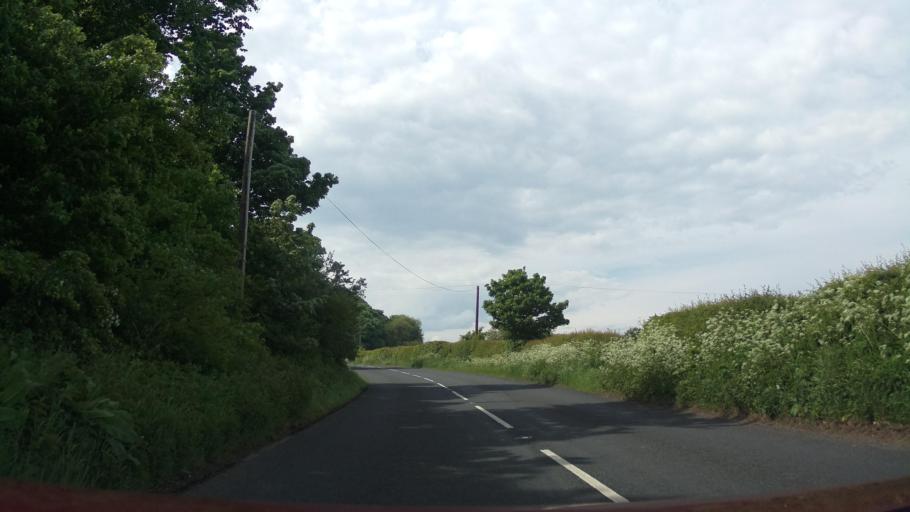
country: GB
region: England
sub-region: Northumberland
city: Alnwick
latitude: 55.4290
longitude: -1.7027
